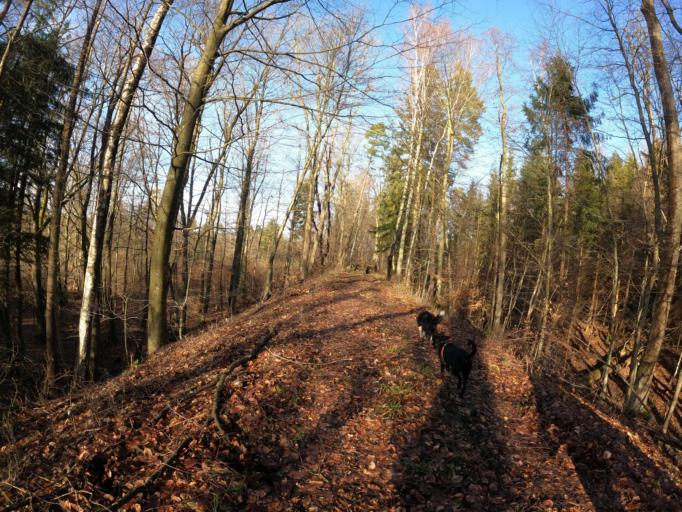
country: PL
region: West Pomeranian Voivodeship
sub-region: Powiat koszalinski
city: Polanow
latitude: 54.2076
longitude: 16.7203
